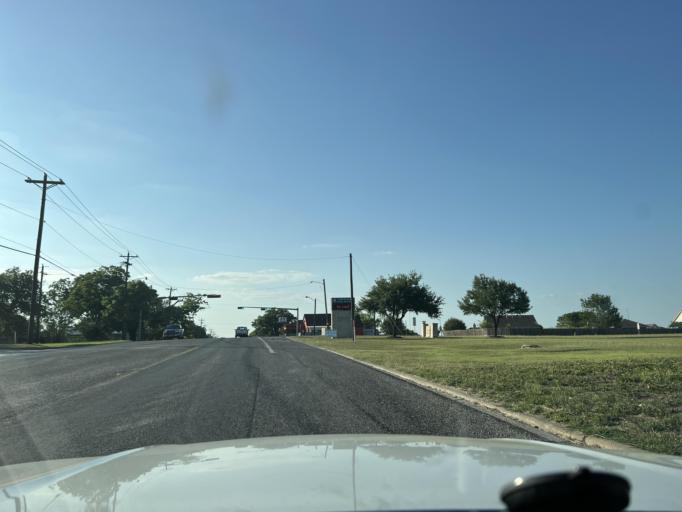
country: US
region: Texas
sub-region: Washington County
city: Brenham
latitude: 30.1805
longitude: -96.4016
